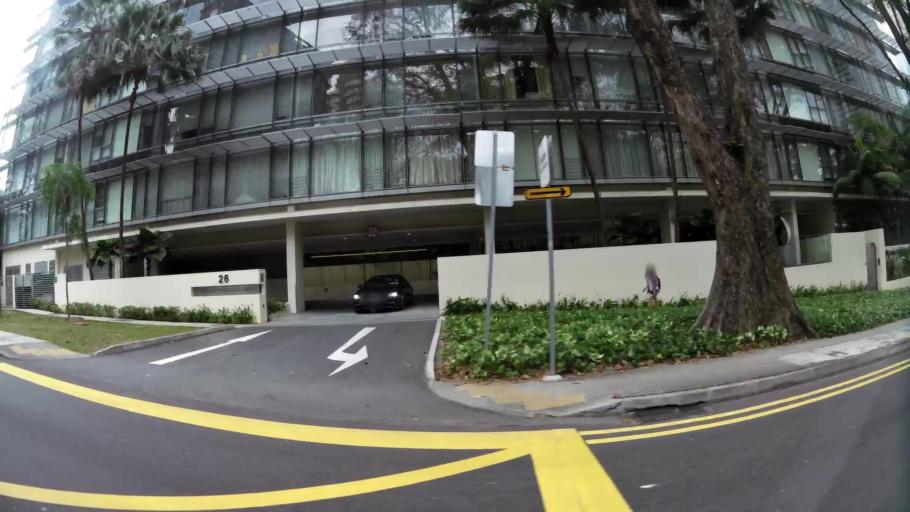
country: SG
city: Singapore
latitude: 1.3024
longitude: 103.8297
